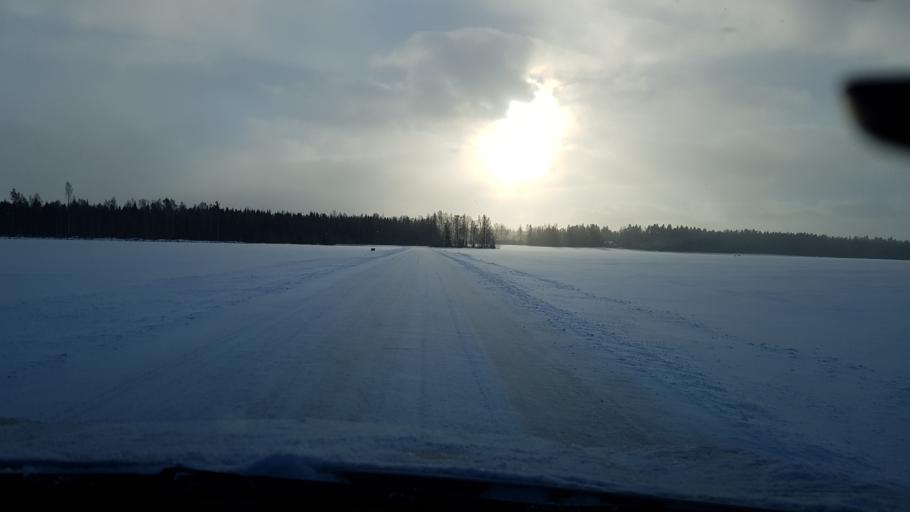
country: EE
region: Harju
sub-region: Nissi vald
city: Turba
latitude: 59.2029
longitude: 24.1401
